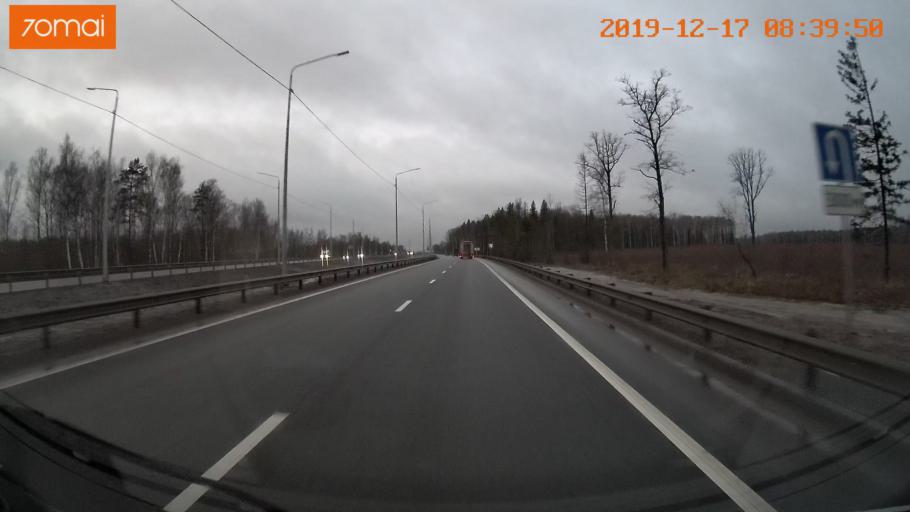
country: RU
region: Vladimir
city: Lakinsk
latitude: 55.9718
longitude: 39.8001
